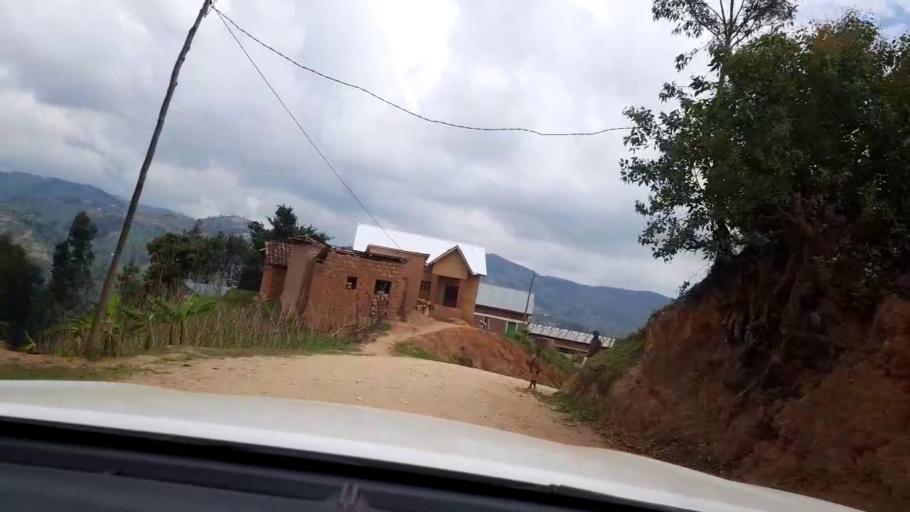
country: RW
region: Western Province
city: Kibuye
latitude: -1.8286
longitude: 29.5457
